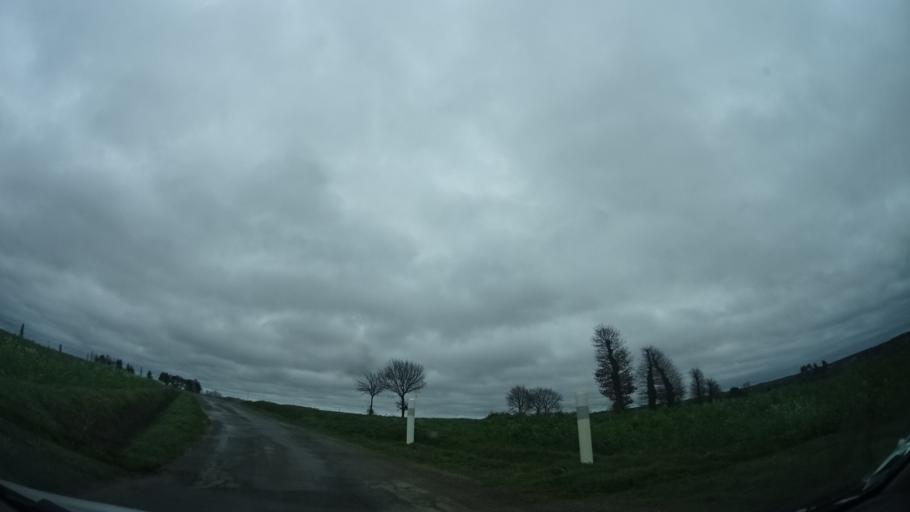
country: FR
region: Brittany
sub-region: Departement d'Ille-et-Vilaine
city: Boisgervilly
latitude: 48.1094
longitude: -2.1010
